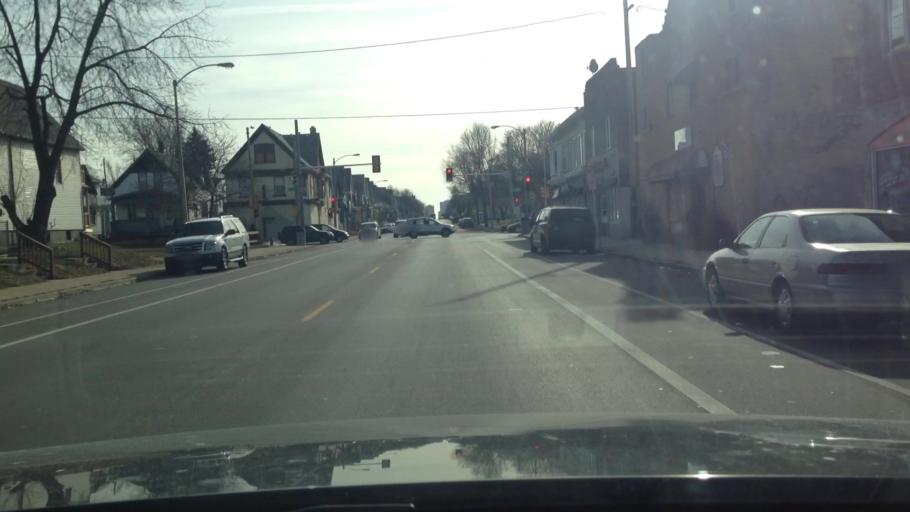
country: US
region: Wisconsin
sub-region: Milwaukee County
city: Shorewood
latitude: 43.0718
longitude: -87.9053
